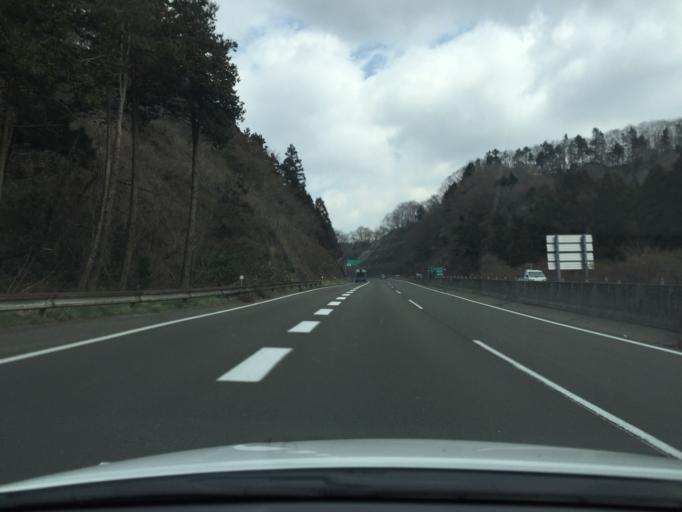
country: JP
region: Miyagi
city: Sendai
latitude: 38.2453
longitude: 140.8172
